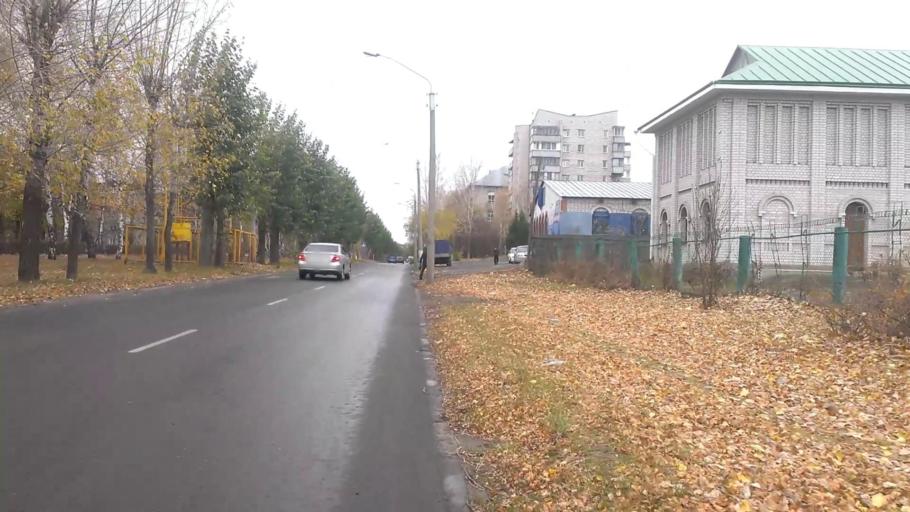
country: RU
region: Altai Krai
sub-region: Gorod Barnaulskiy
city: Barnaul
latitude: 53.3611
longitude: 83.7144
